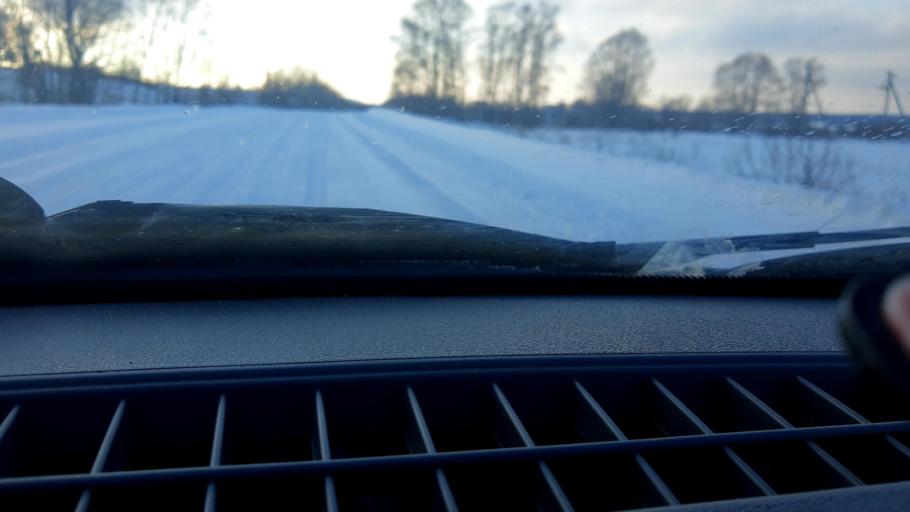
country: RU
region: Bashkortostan
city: Asanovo
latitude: 55.1418
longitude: 55.6351
